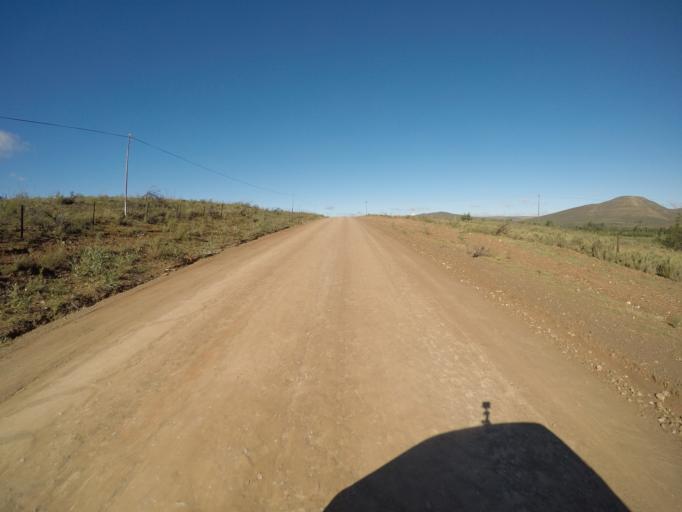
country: ZA
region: Western Cape
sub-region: Overberg District Municipality
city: Caledon
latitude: -34.0596
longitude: 19.6220
